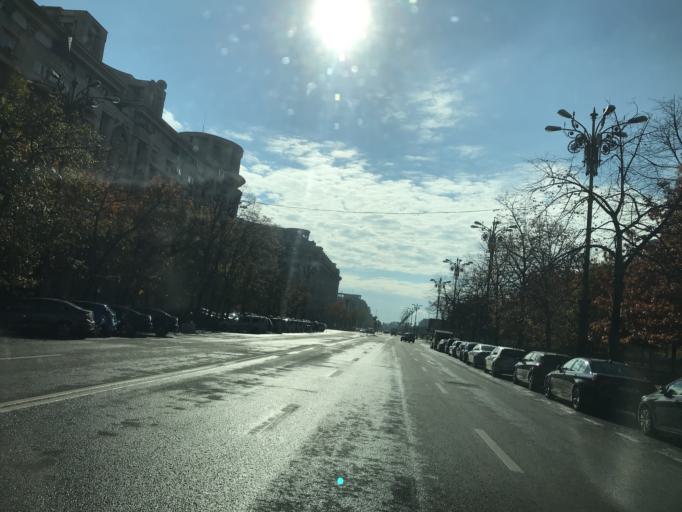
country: RO
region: Bucuresti
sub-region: Municipiul Bucuresti
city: Bucuresti
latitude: 44.4318
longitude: 26.0913
